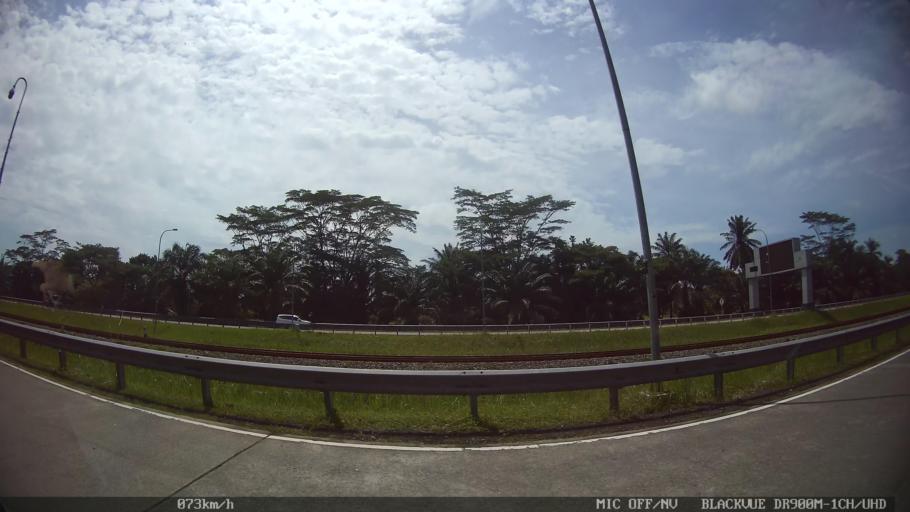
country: ID
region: North Sumatra
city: Percut
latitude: 3.6162
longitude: 98.8595
